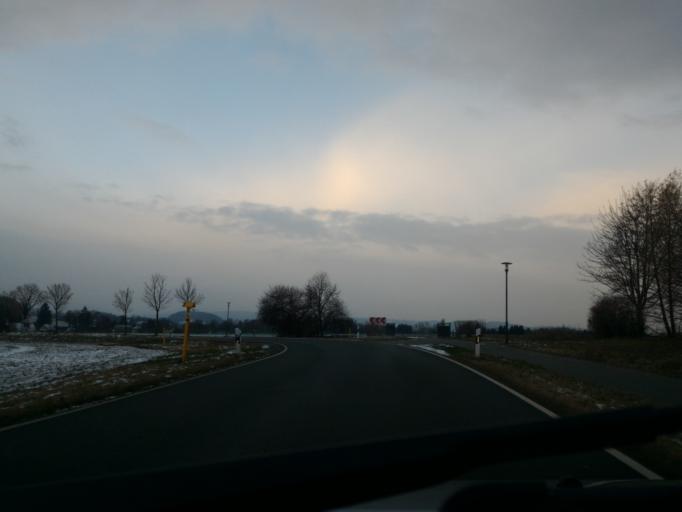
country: DE
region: Saxony
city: Leutersdorf
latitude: 50.9471
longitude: 14.6293
